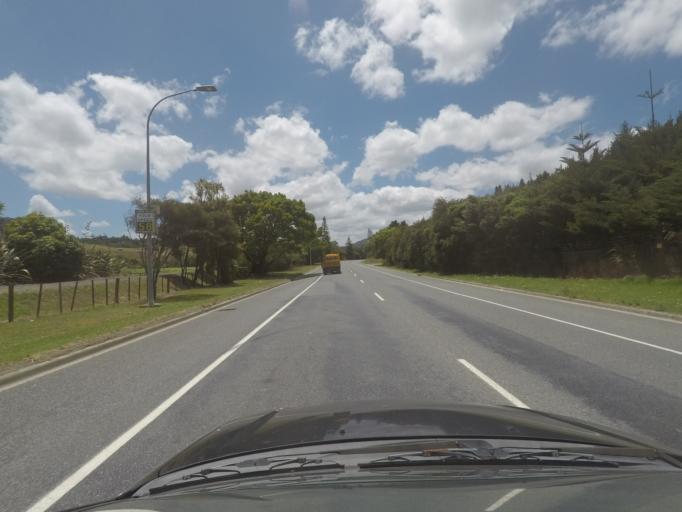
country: NZ
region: Northland
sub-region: Whangarei
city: Whangarei
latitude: -35.7486
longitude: 174.3206
